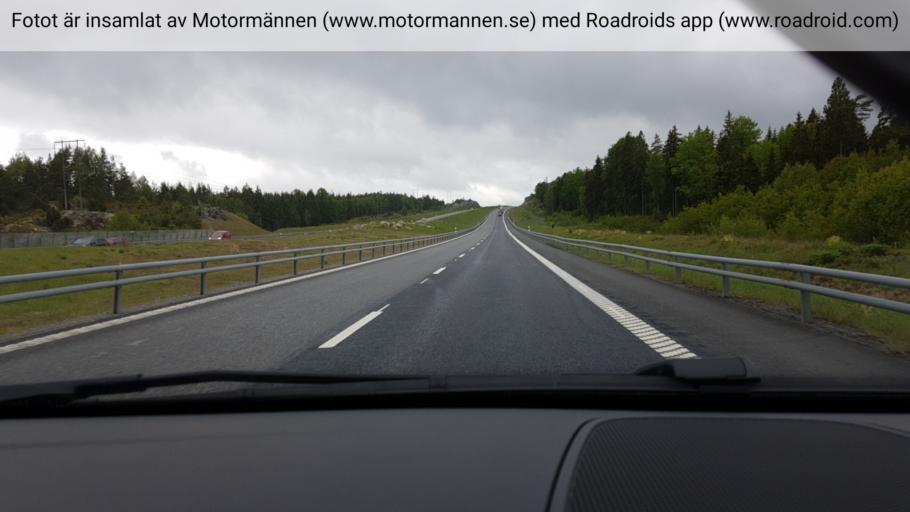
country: SE
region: Stockholm
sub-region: Nynashamns Kommun
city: Osmo
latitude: 59.0550
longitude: 18.0039
